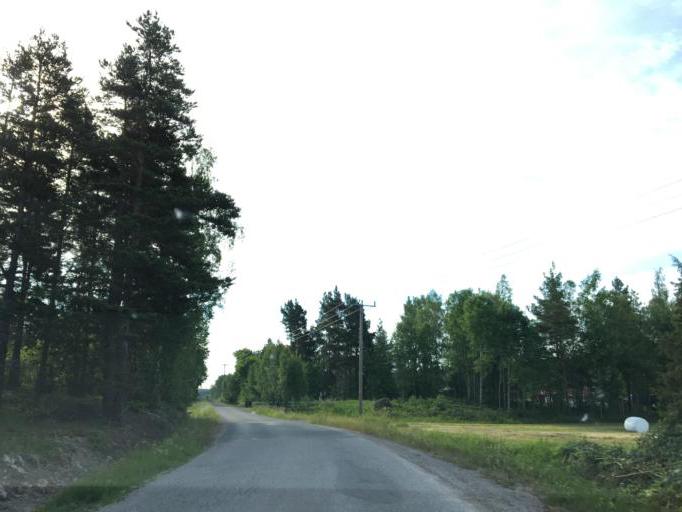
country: SE
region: Soedermanland
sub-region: Eskilstuna Kommun
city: Kvicksund
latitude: 59.4315
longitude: 16.3667
